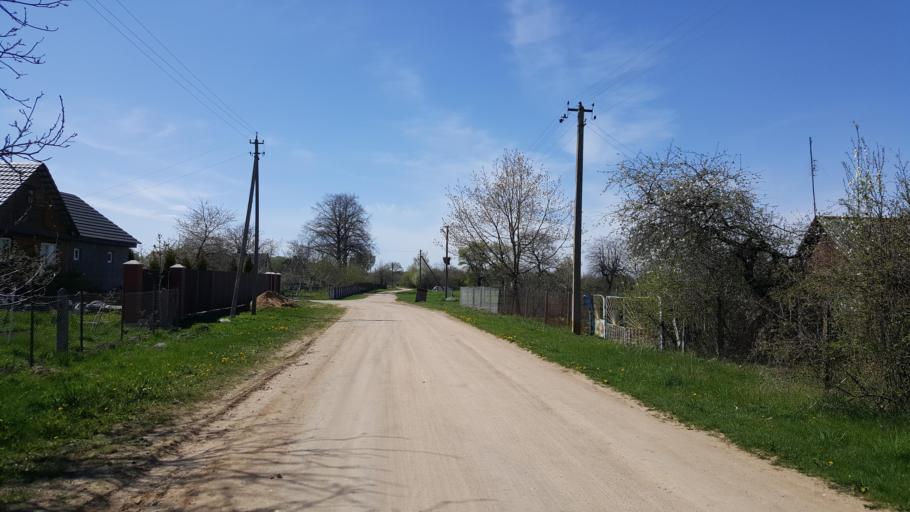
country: BY
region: Brest
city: Vysokaye
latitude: 52.3531
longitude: 23.4419
